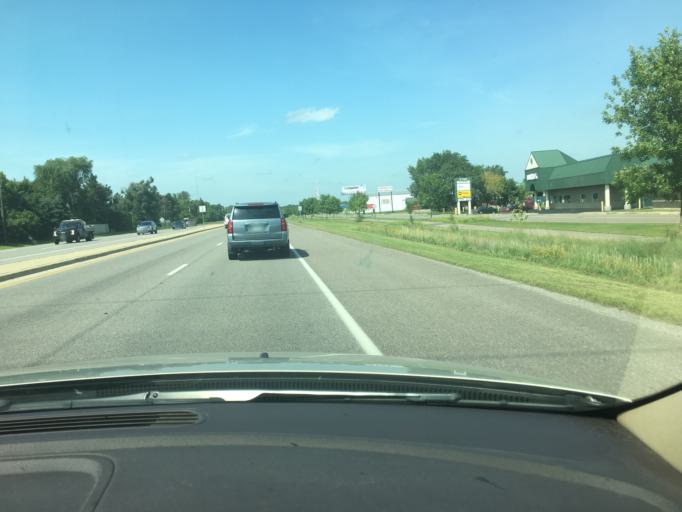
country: US
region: Minnesota
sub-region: Stearns County
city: Saint Cloud
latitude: 45.5224
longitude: -94.1615
